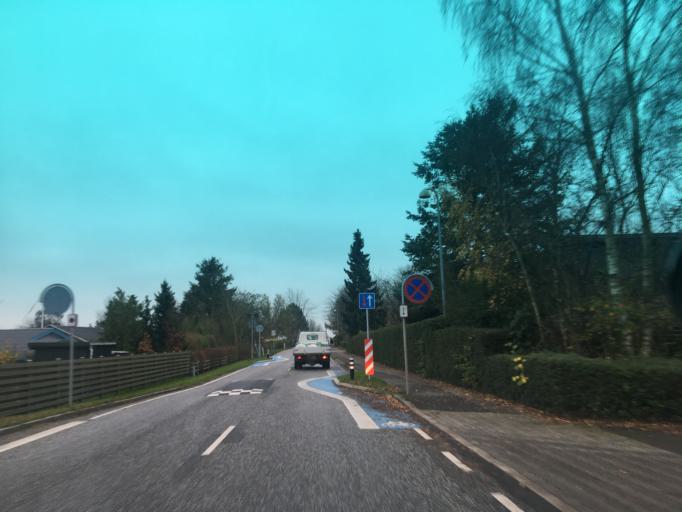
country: DK
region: Zealand
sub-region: Slagelse Kommune
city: Slagelse
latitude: 55.3096
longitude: 11.3951
